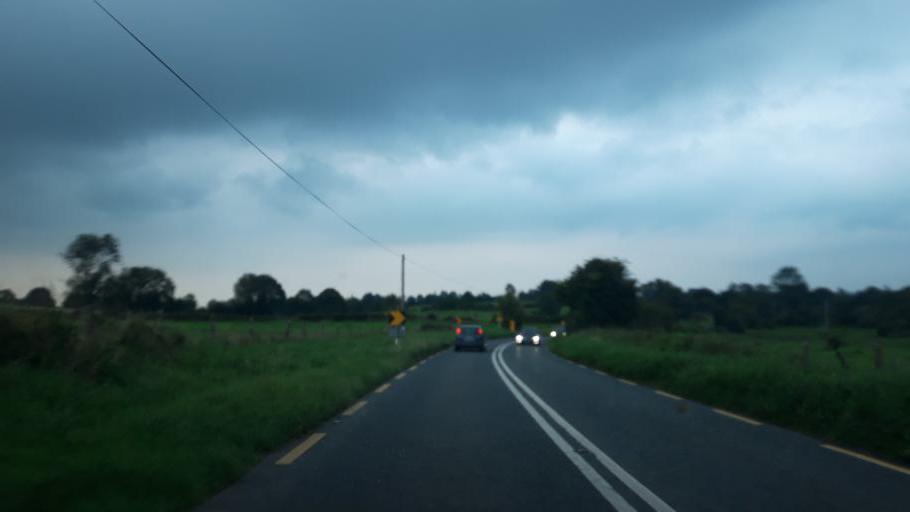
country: IE
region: Leinster
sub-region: Kilkenny
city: Thomastown
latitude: 52.5591
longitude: -7.1241
